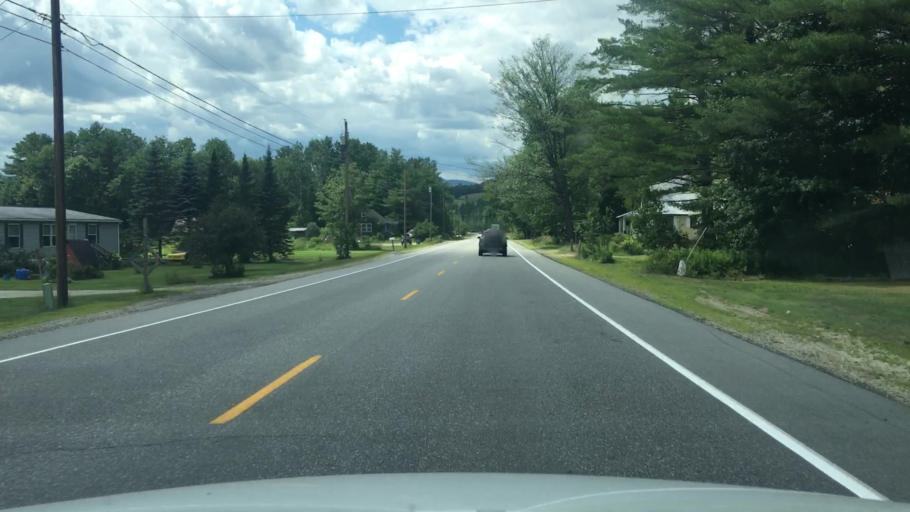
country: US
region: Maine
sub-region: Oxford County
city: Bethel
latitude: 44.4175
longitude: -70.7402
